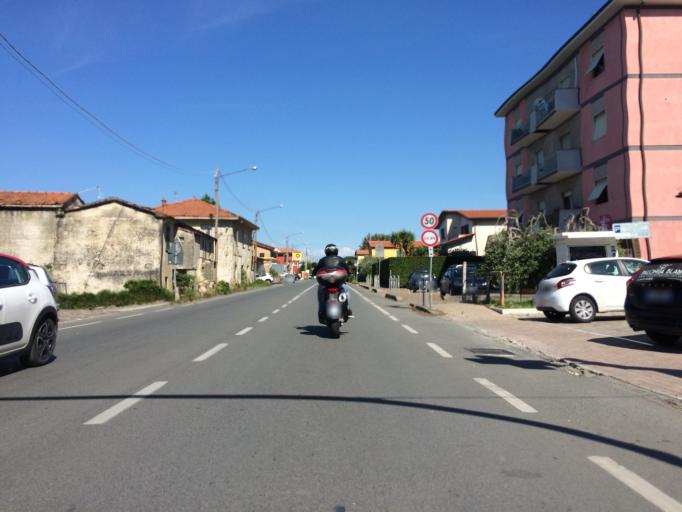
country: IT
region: Liguria
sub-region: Provincia di La Spezia
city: Casano-Dogana-Isola
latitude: 44.0668
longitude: 10.0305
